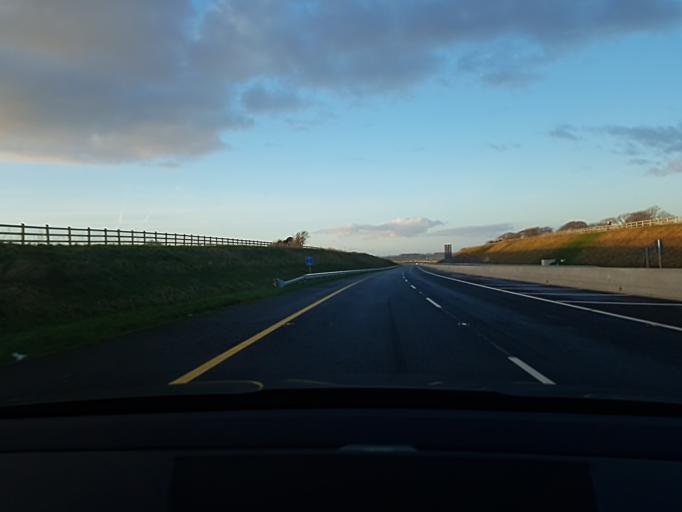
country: IE
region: Connaught
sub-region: County Galway
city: Tuam
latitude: 53.4084
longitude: -8.8255
